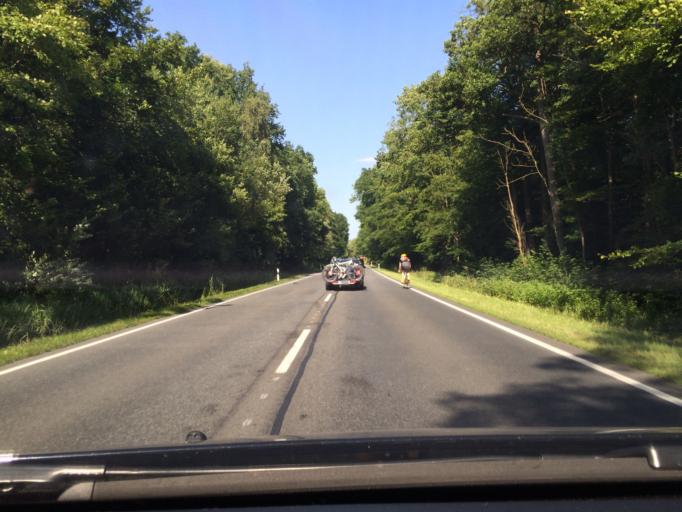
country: DE
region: Mecklenburg-Vorpommern
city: Gelbensande
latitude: 54.2179
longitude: 12.3533
